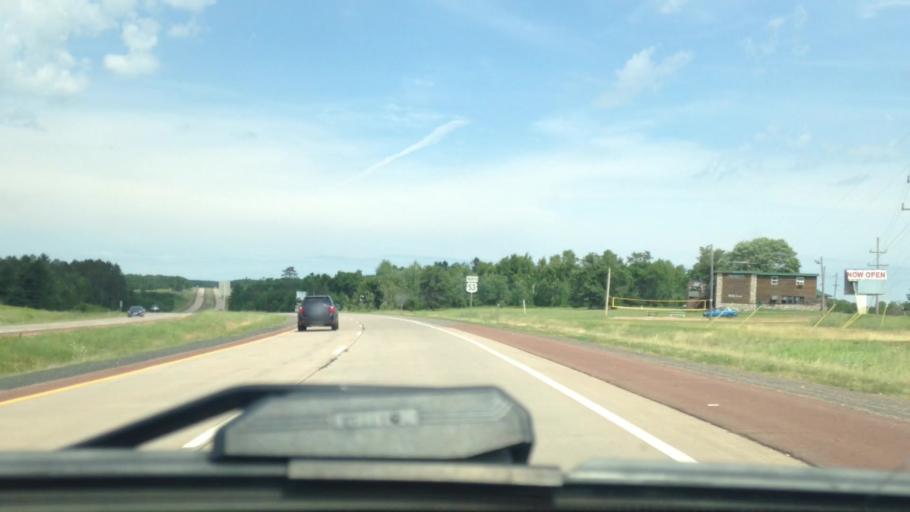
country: US
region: Wisconsin
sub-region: Douglas County
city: Lake Nebagamon
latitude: 46.3201
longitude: -91.8127
